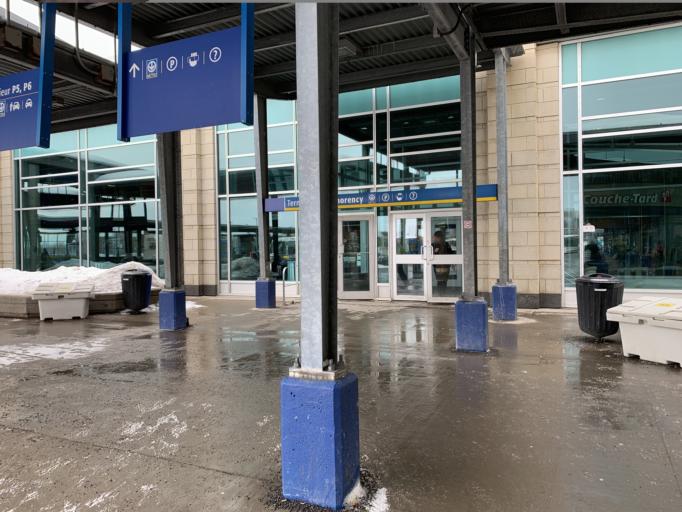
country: CA
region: Quebec
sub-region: Laval
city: Laval
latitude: 45.5582
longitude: -73.7210
